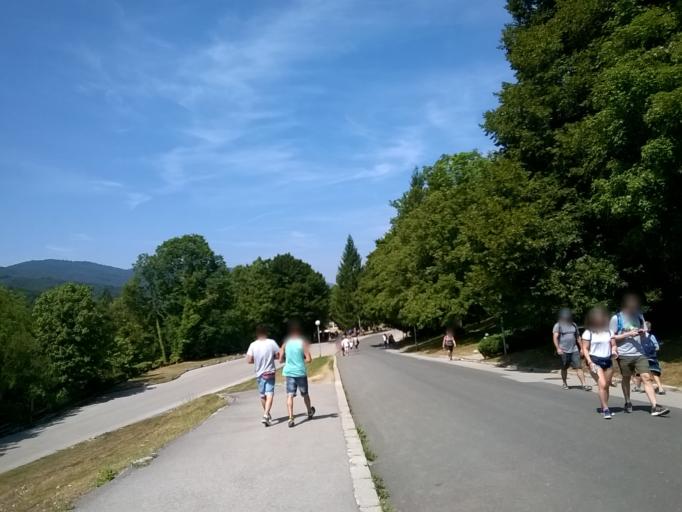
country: HR
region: Licko-Senjska
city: Jezerce
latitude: 44.8812
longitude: 15.6199
